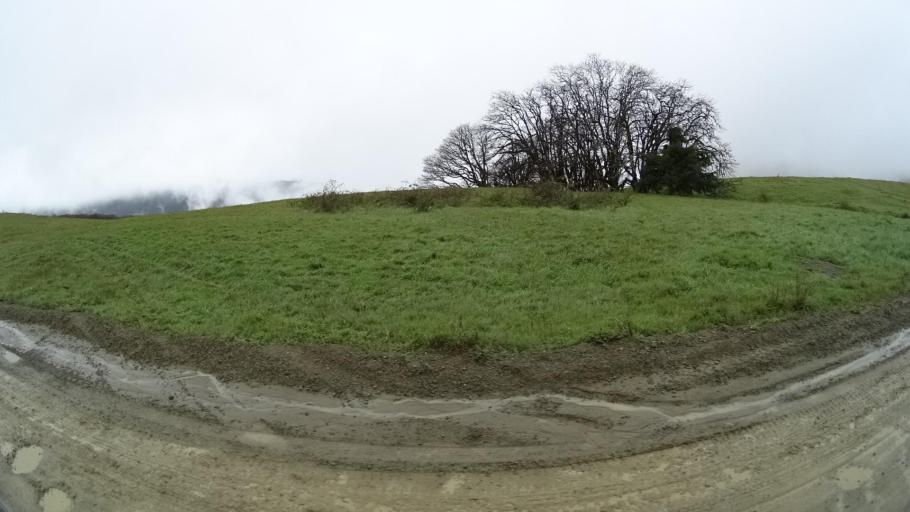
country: US
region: California
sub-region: Humboldt County
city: Westhaven-Moonstone
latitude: 41.1436
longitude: -123.8663
